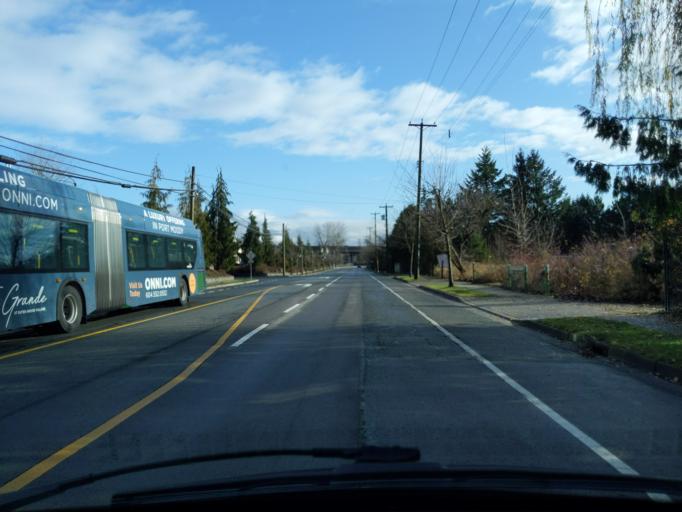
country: CA
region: British Columbia
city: Pitt Meadows
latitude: 49.2172
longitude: -122.6742
